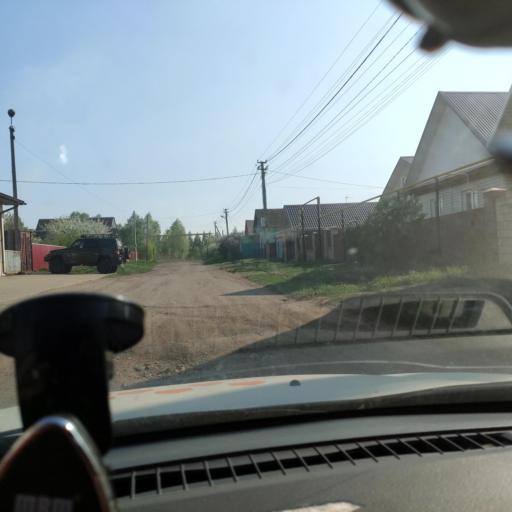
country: RU
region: Bashkortostan
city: Iglino
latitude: 54.7967
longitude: 56.2663
